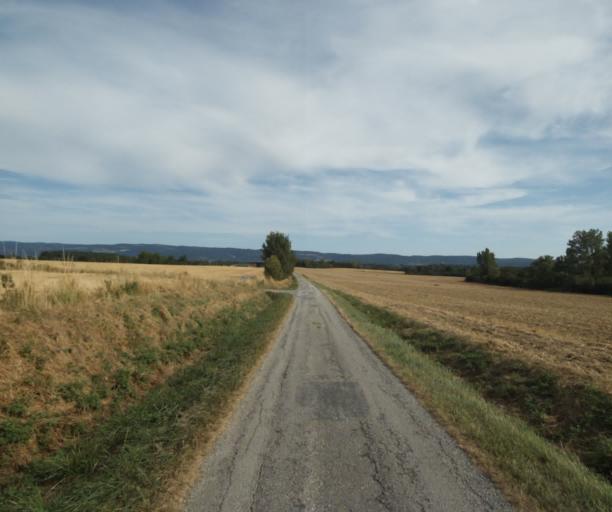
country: FR
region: Midi-Pyrenees
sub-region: Departement du Tarn
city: Puylaurens
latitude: 43.5301
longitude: 2.0364
